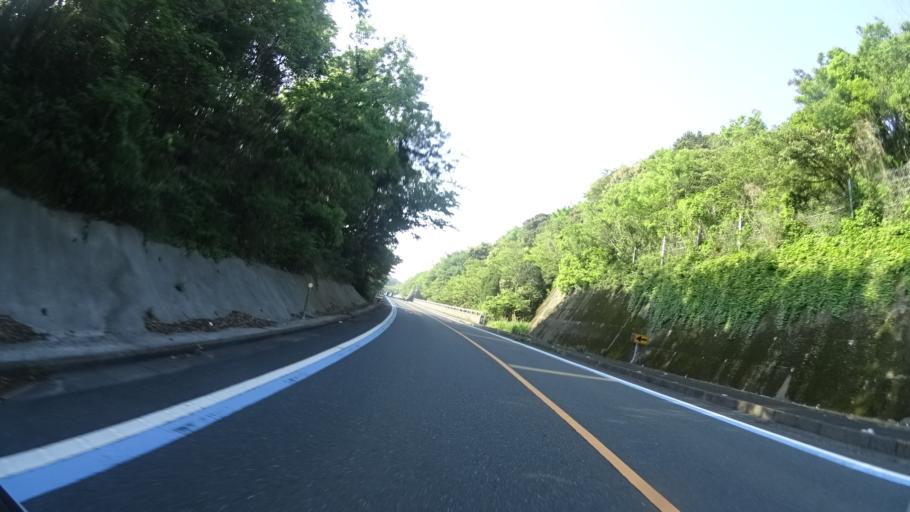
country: JP
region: Ehime
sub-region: Nishiuwa-gun
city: Ikata-cho
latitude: 33.4629
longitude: 132.2717
